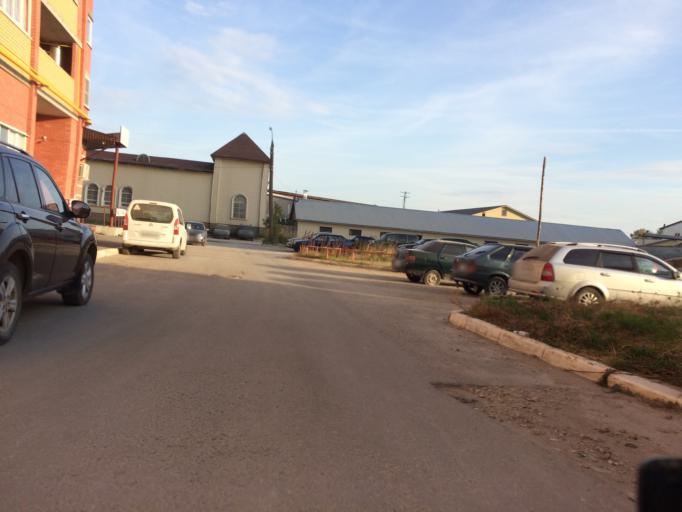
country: RU
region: Mariy-El
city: Yoshkar-Ola
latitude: 56.6281
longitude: 47.8524
